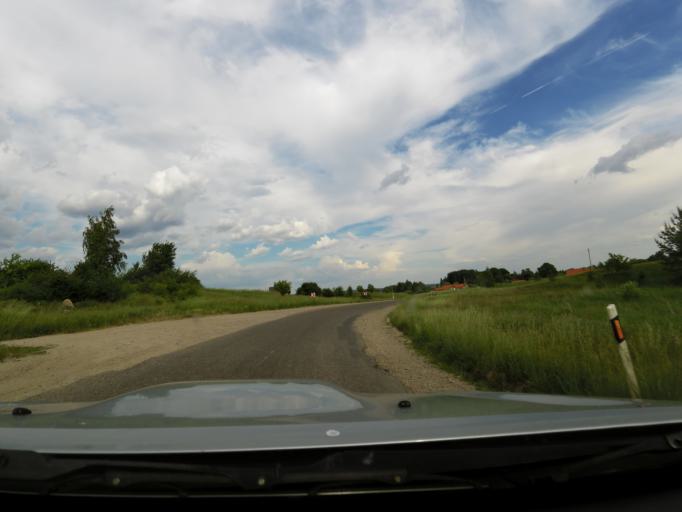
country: LT
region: Vilnius County
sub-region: Vilniaus Rajonas
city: Vievis
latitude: 54.7578
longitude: 24.7864
